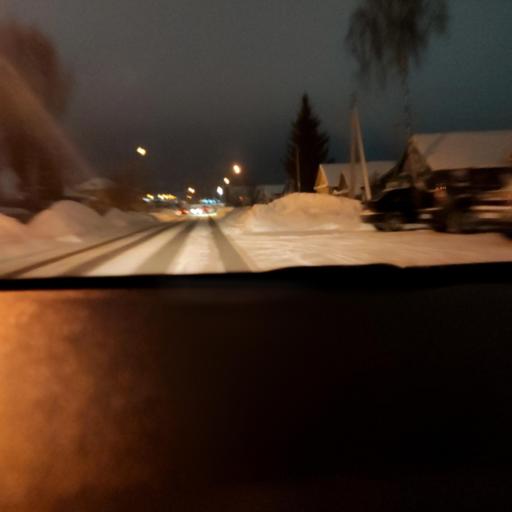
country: RU
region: Tatarstan
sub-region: Chistopol'skiy Rayon
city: Chistopol'
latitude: 55.3568
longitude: 50.6622
